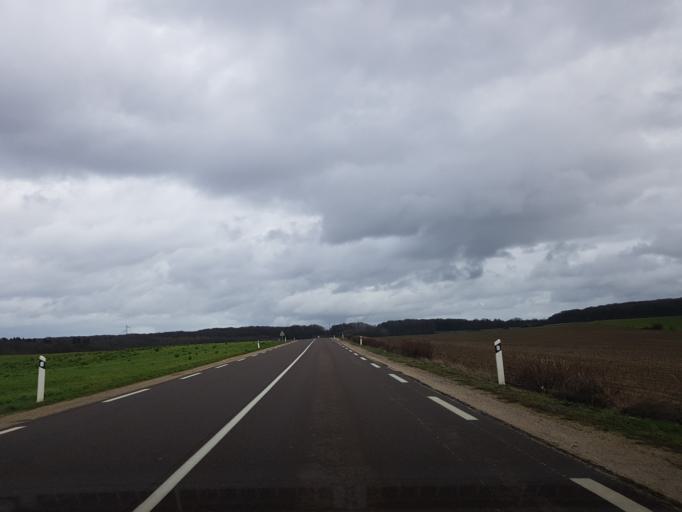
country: FR
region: Franche-Comte
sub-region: Departement de la Haute-Saone
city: Scey-sur-Saone-et-Saint-Albin
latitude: 47.7092
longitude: 5.9104
